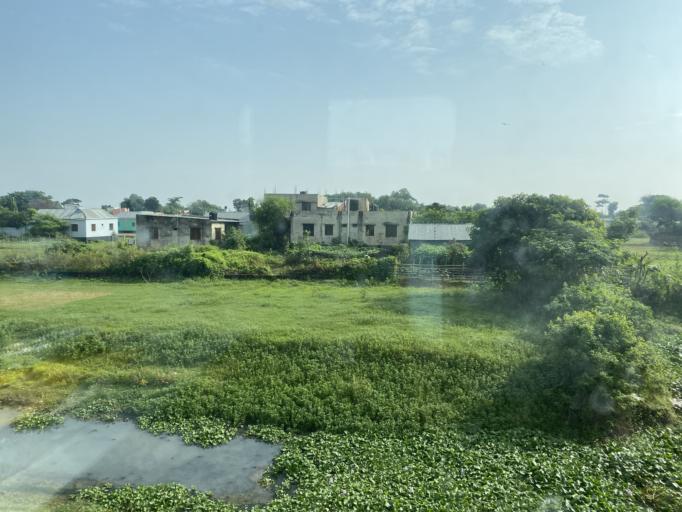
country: BD
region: Chittagong
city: Nabinagar
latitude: 23.9599
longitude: 91.1191
